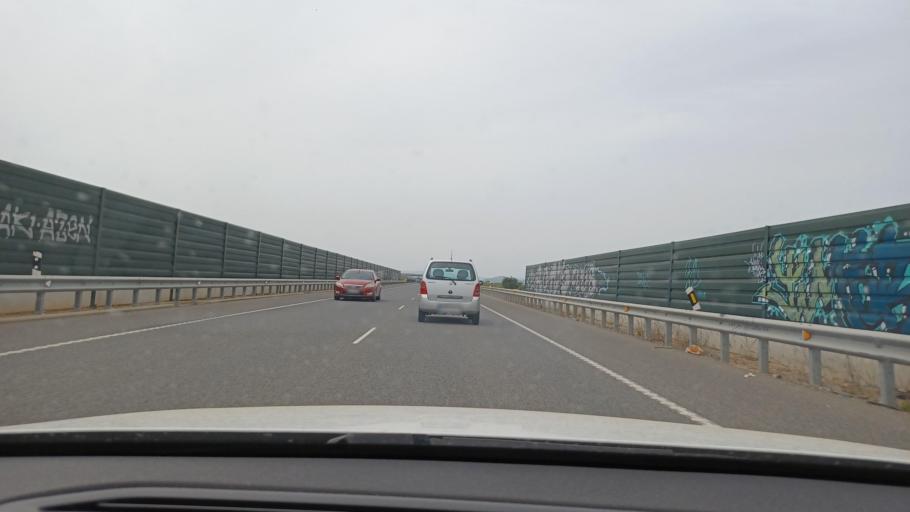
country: ES
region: Catalonia
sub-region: Provincia de Tarragona
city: Alcanar
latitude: 40.5134
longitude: 0.4825
